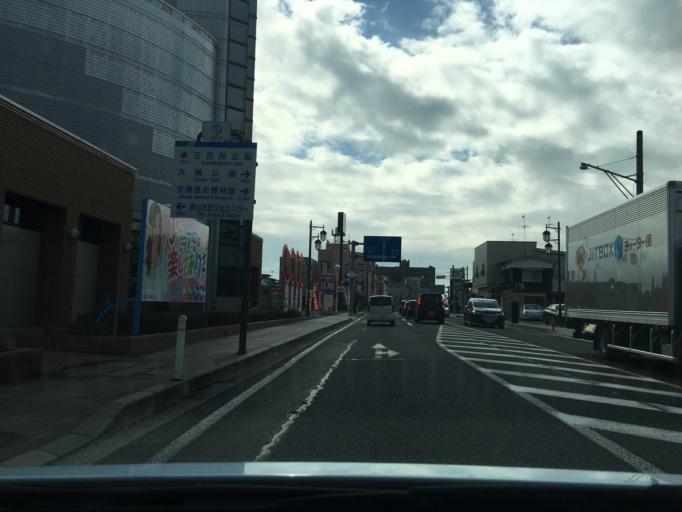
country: JP
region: Fukushima
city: Koriyama
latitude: 37.3935
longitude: 140.3551
